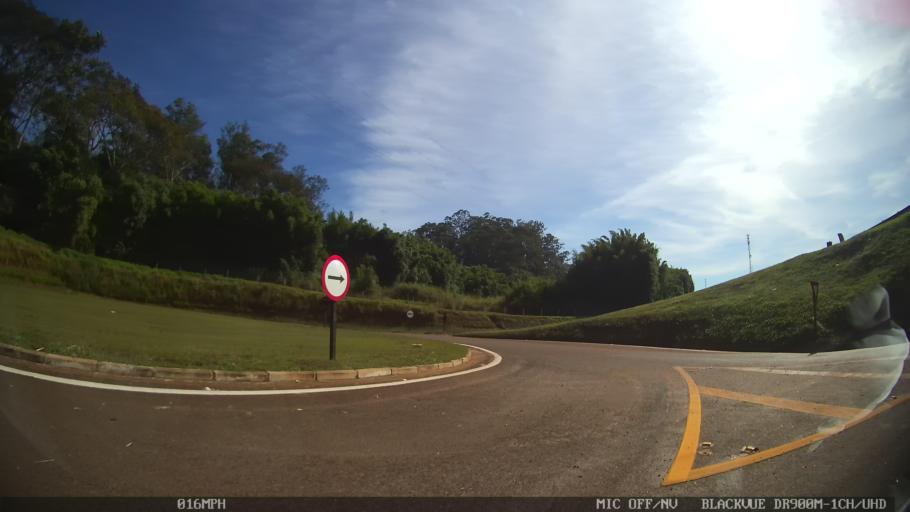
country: BR
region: Sao Paulo
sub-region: Araras
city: Araras
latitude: -22.2740
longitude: -47.3926
